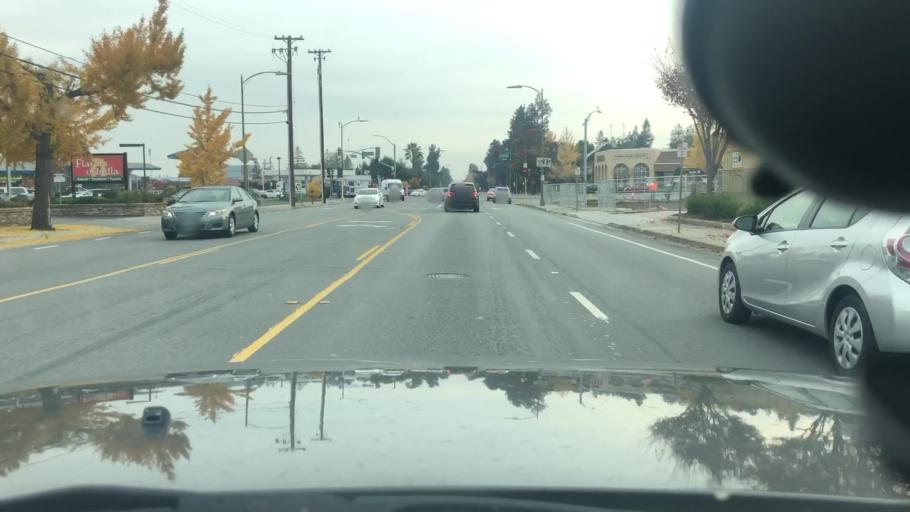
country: US
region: California
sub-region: Santa Clara County
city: Campbell
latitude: 37.3159
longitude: -121.9773
